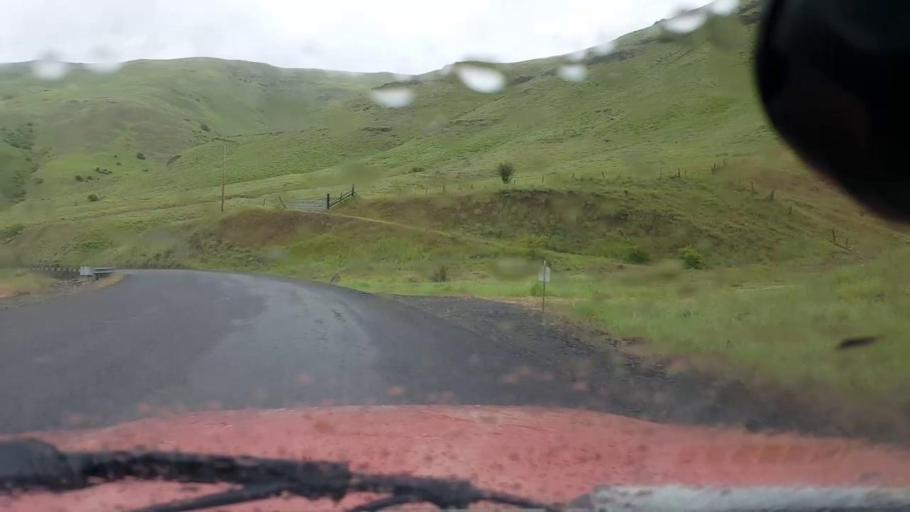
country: US
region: Washington
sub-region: Asotin County
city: Asotin
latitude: 46.0410
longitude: -117.2915
